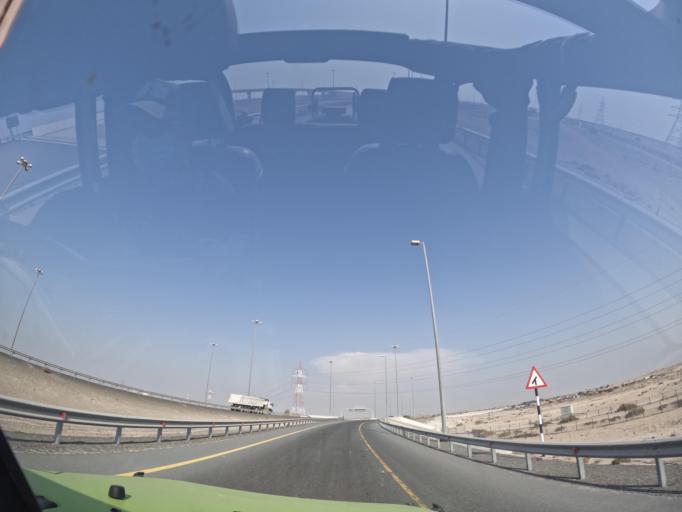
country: AE
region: Abu Dhabi
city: Abu Dhabi
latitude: 24.6779
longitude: 54.8263
